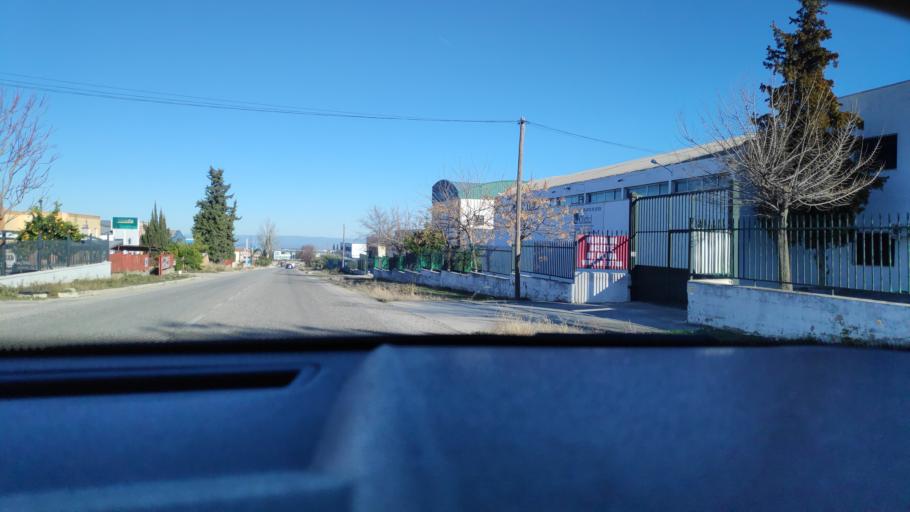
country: ES
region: Andalusia
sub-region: Provincia de Jaen
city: Mancha Real
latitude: 37.8020
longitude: -3.6103
